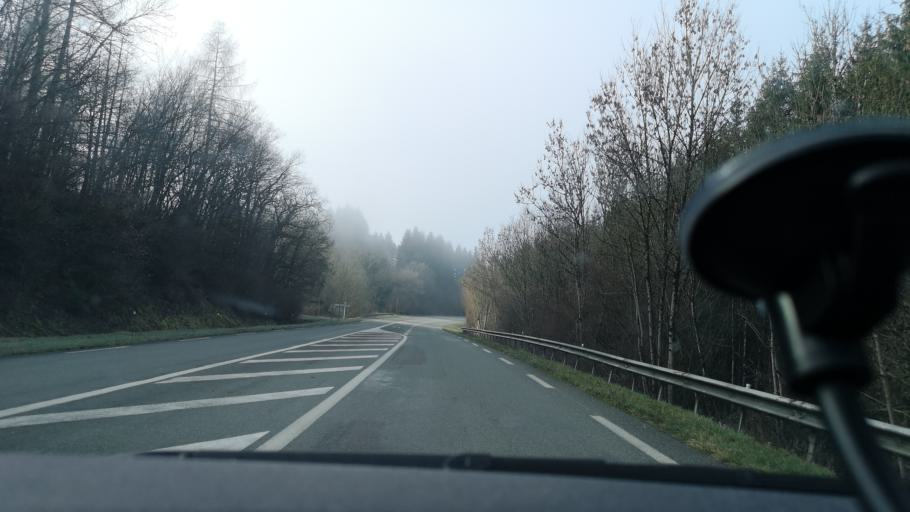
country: FR
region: Franche-Comte
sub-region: Departement du Doubs
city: Clerval
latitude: 47.4120
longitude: 6.5410
